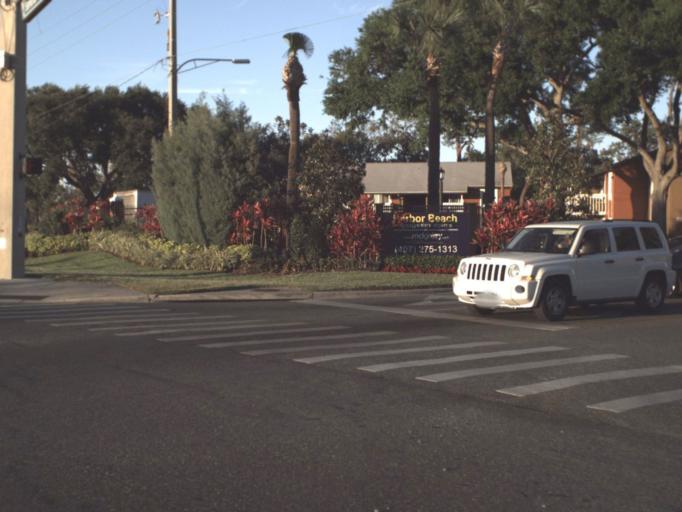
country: US
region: Florida
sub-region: Orange County
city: Conway
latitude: 28.5057
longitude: -81.3101
